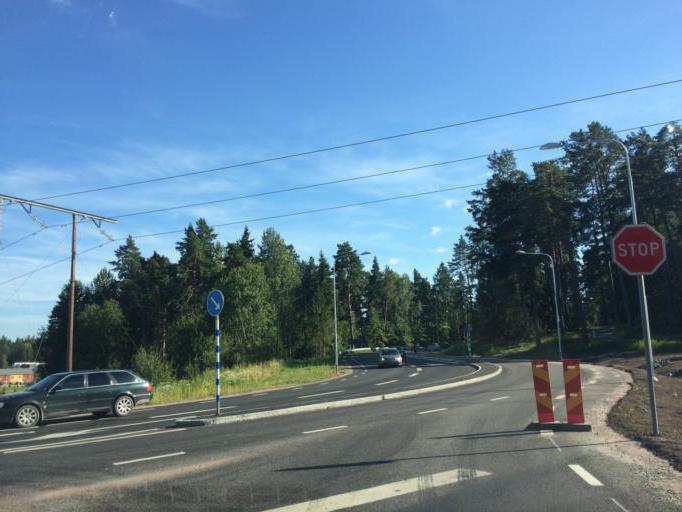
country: SE
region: Stockholm
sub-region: Upplands Vasby Kommun
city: Upplands Vaesby
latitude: 59.5112
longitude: 17.9503
